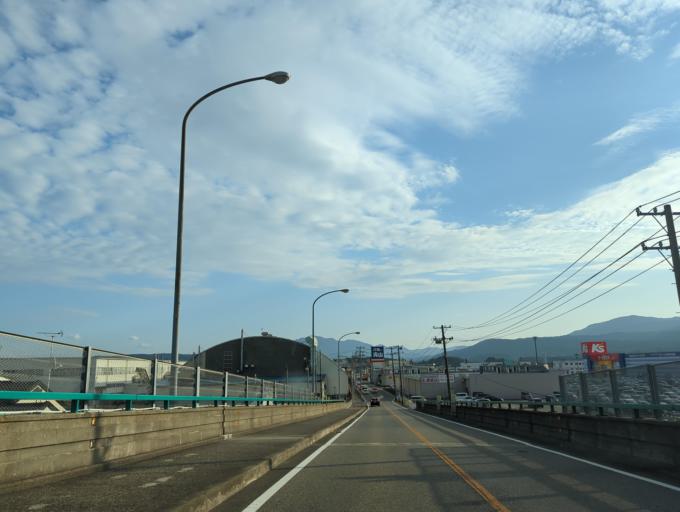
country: JP
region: Niigata
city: Kashiwazaki
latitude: 37.3645
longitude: 138.5634
